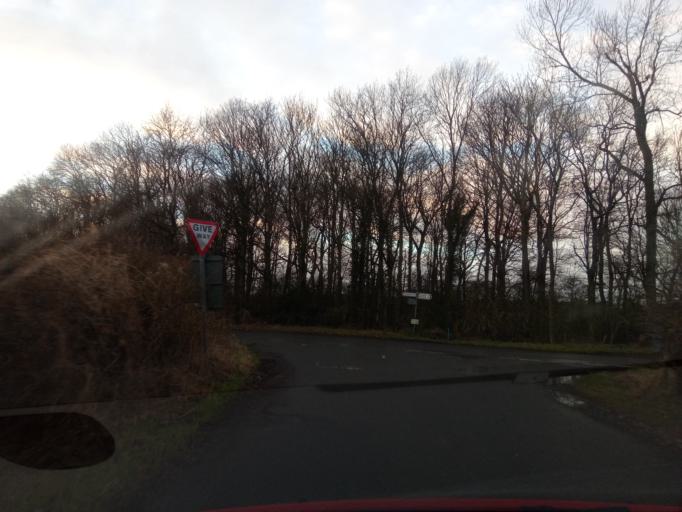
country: GB
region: England
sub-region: Northumberland
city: Ponteland
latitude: 55.0849
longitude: -1.7600
